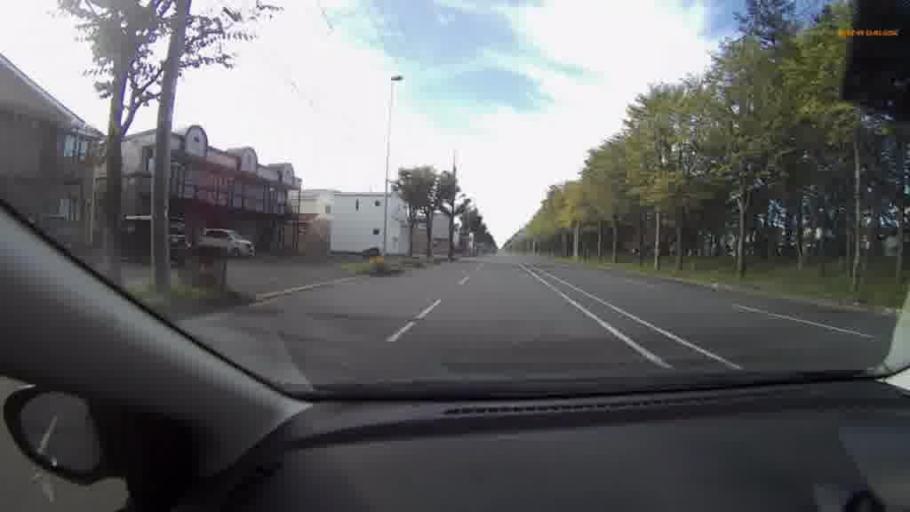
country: JP
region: Hokkaido
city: Kushiro
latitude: 43.0209
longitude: 144.4160
